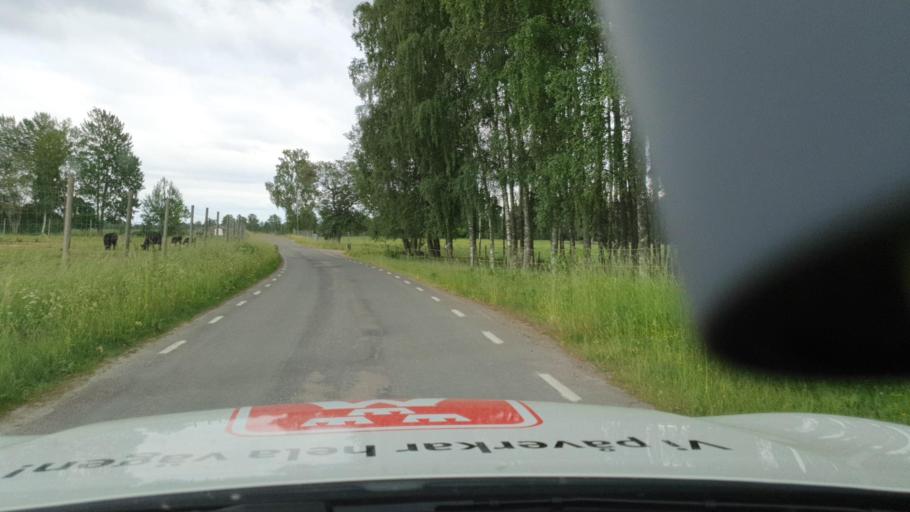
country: SE
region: Vaestra Goetaland
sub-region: Tidaholms Kommun
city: Olofstorp
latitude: 58.1733
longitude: 14.1611
